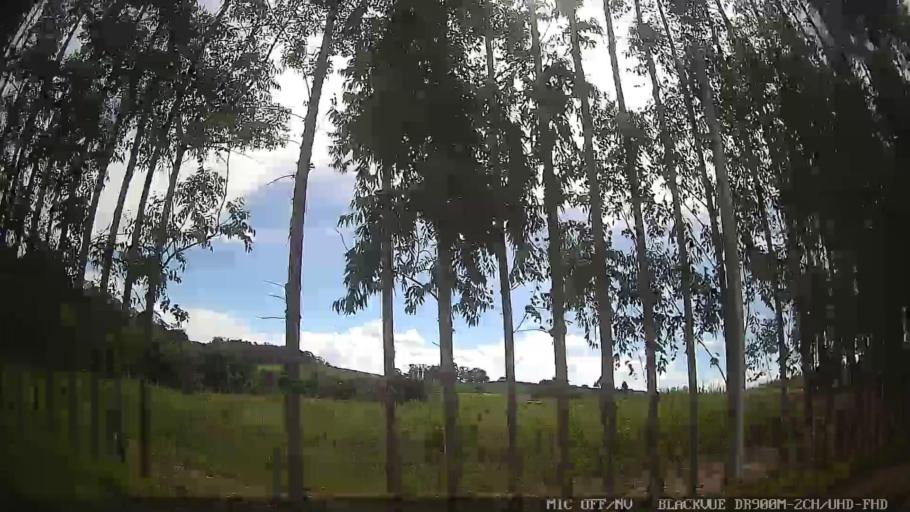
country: BR
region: Sao Paulo
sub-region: Conchas
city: Conchas
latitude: -22.9610
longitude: -47.9815
